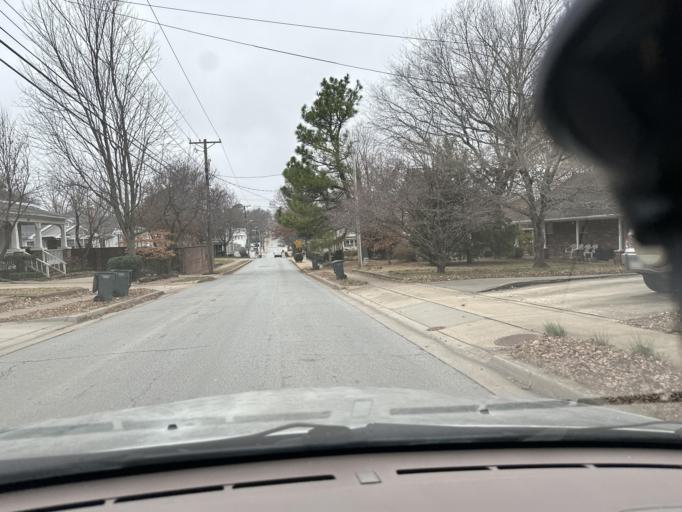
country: US
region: Arkansas
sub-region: Washington County
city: Fayetteville
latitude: 36.0699
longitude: -94.1551
